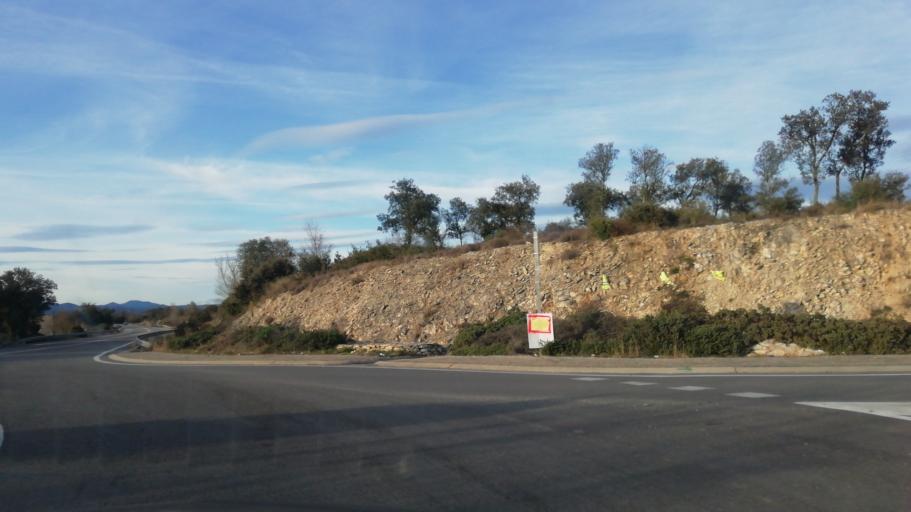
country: FR
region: Languedoc-Roussillon
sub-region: Departement du Gard
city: Quissac
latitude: 43.8922
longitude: 4.0118
